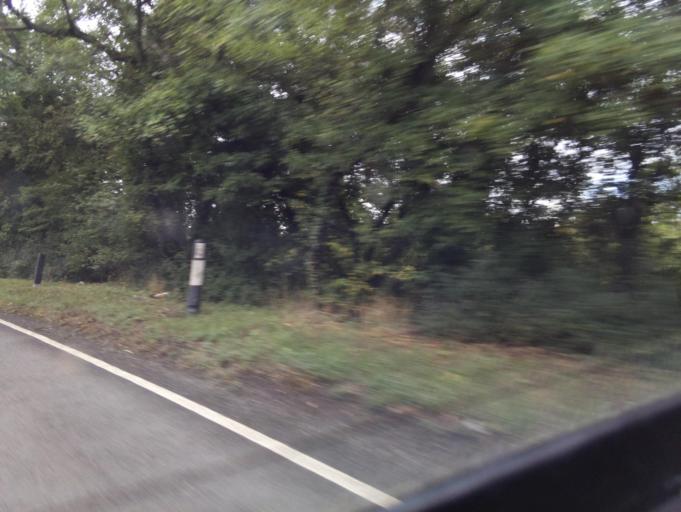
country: GB
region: England
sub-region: Worcestershire
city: Droitwich
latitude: 52.3040
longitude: -2.1749
